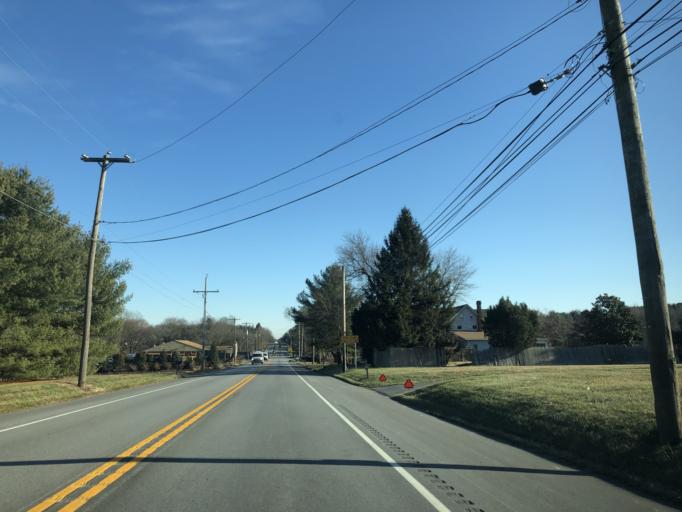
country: US
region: Delaware
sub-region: New Castle County
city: Hockessin
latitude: 39.7958
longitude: -75.7175
